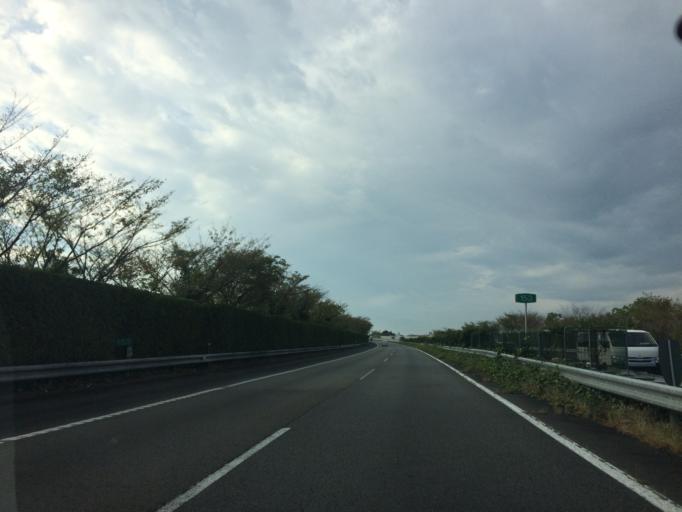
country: JP
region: Shizuoka
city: Shizuoka-shi
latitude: 35.0101
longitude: 138.4346
